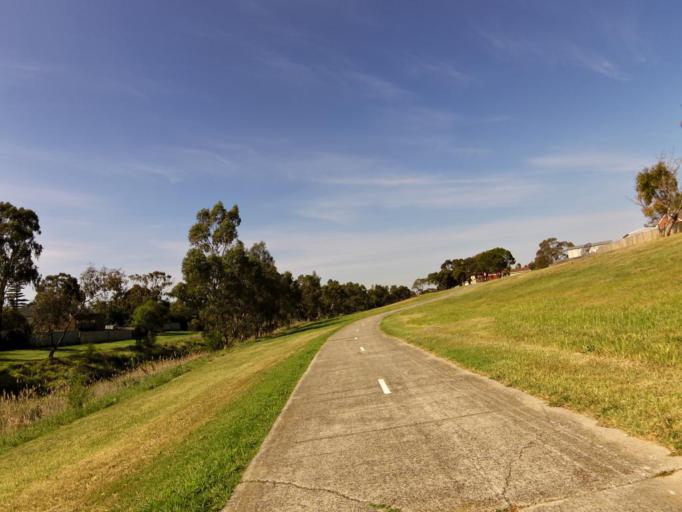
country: AU
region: Victoria
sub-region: Brimbank
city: Sunshine West
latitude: -37.8007
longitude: 144.8236
